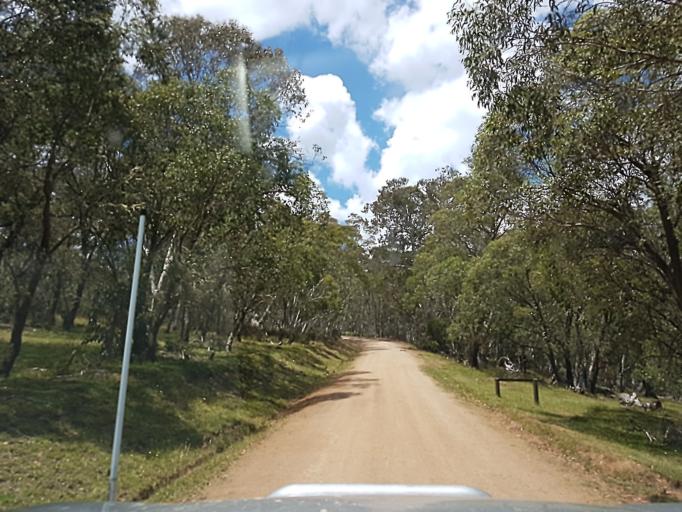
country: AU
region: New South Wales
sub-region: Snowy River
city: Jindabyne
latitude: -36.8971
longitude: 148.0914
